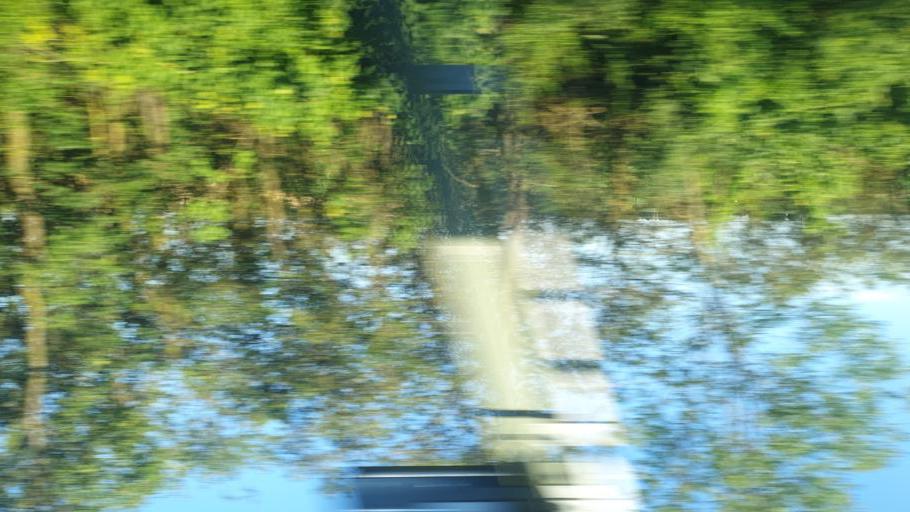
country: DE
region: Bavaria
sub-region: Regierungsbezirk Unterfranken
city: Iphofen
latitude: 49.6912
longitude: 10.2682
